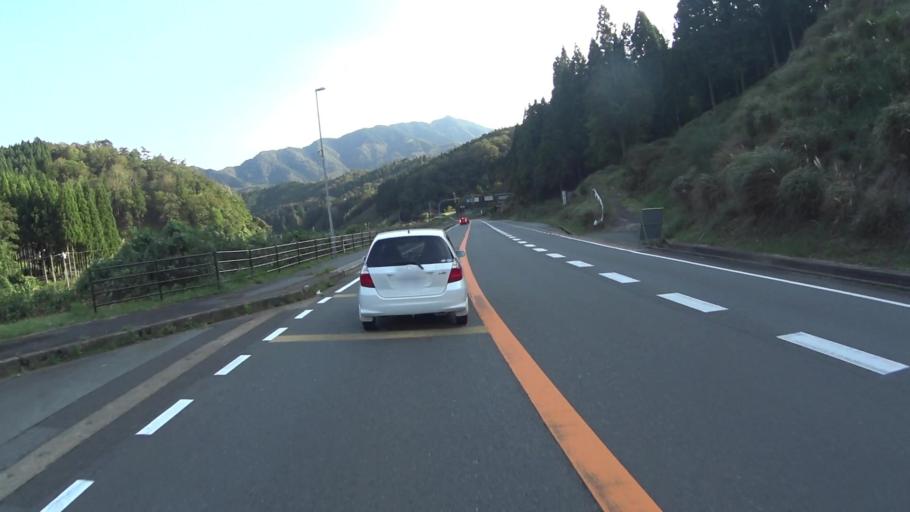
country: JP
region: Kyoto
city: Fukuchiyama
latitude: 35.4336
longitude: 135.0678
